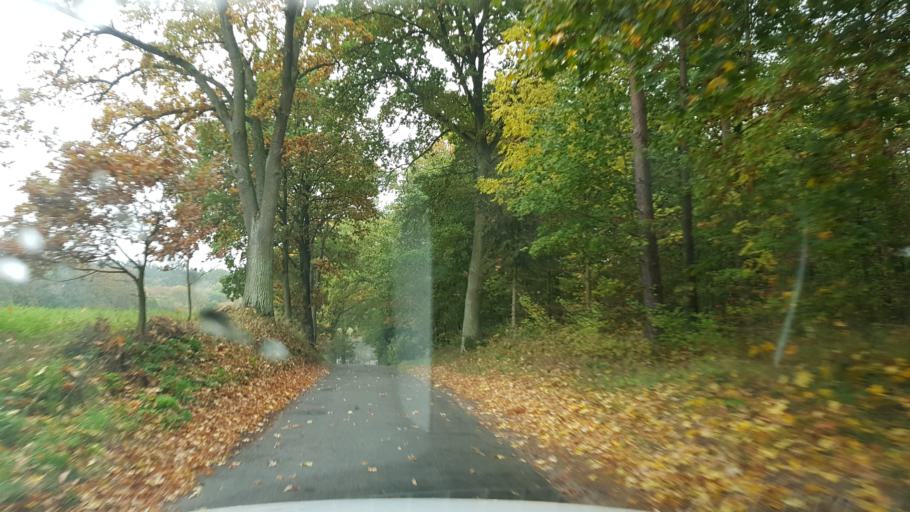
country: PL
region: West Pomeranian Voivodeship
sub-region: Powiat mysliborski
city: Barlinek
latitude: 53.0285
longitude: 15.2286
